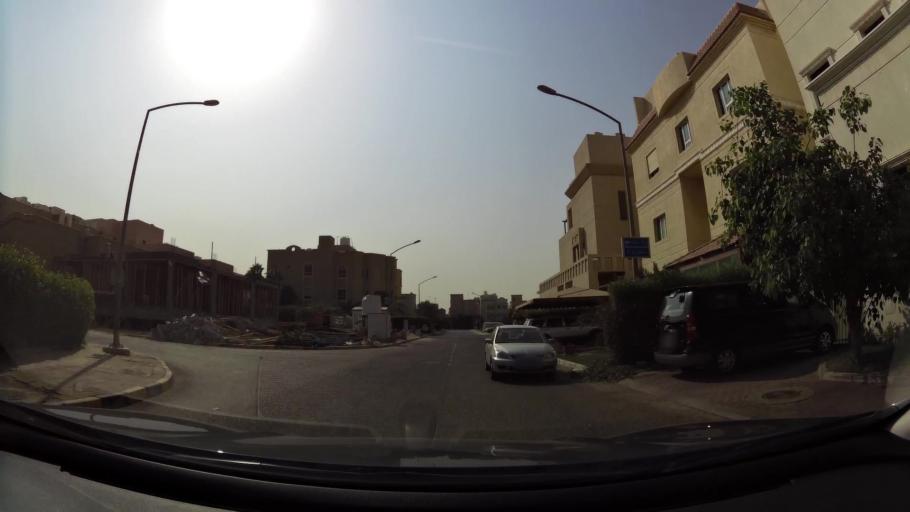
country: KW
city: Bayan
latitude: 29.2864
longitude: 48.0499
